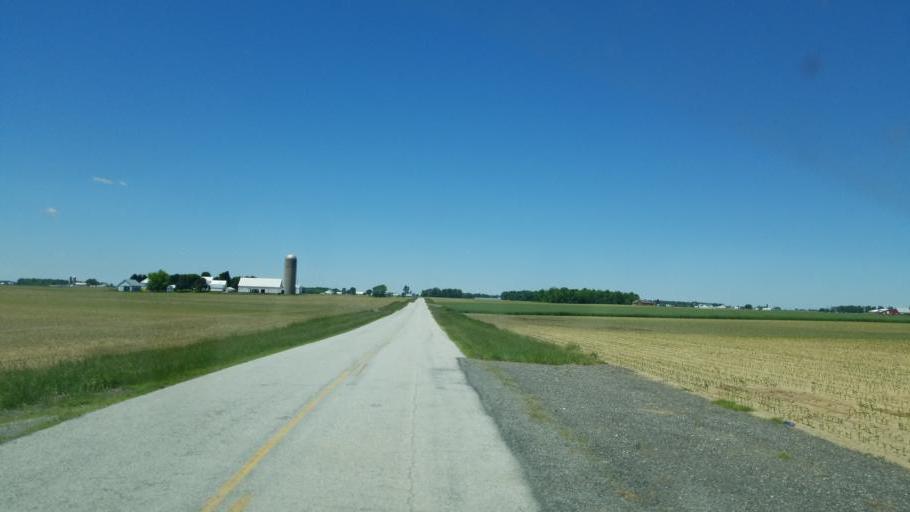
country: US
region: Ohio
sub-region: Auglaize County
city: Minster
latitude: 40.3856
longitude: -84.4448
